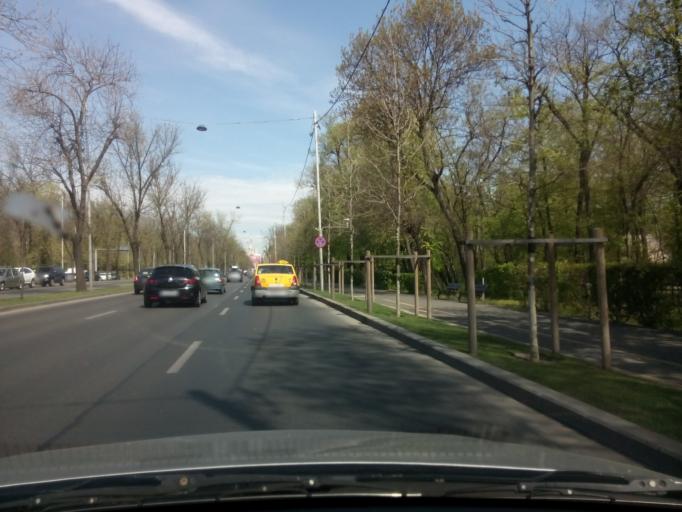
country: RO
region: Bucuresti
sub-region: Municipiul Bucuresti
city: Bucuresti
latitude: 44.4679
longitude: 26.0780
